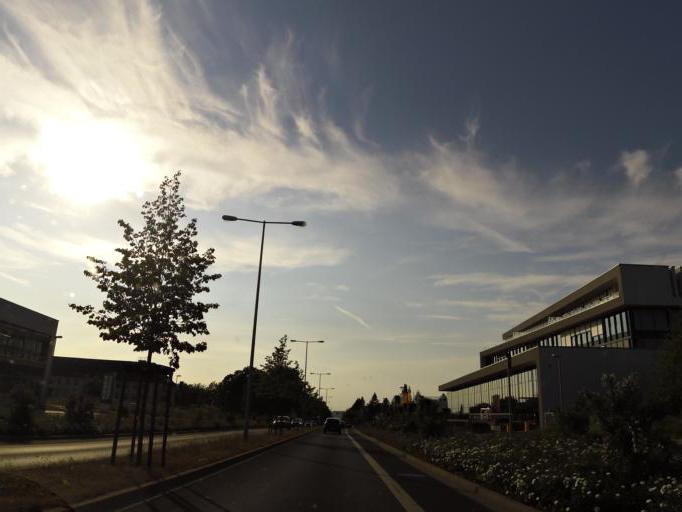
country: DE
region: Bavaria
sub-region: Regierungsbezirk Unterfranken
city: Aschaffenburg
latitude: 49.9637
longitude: 9.1741
